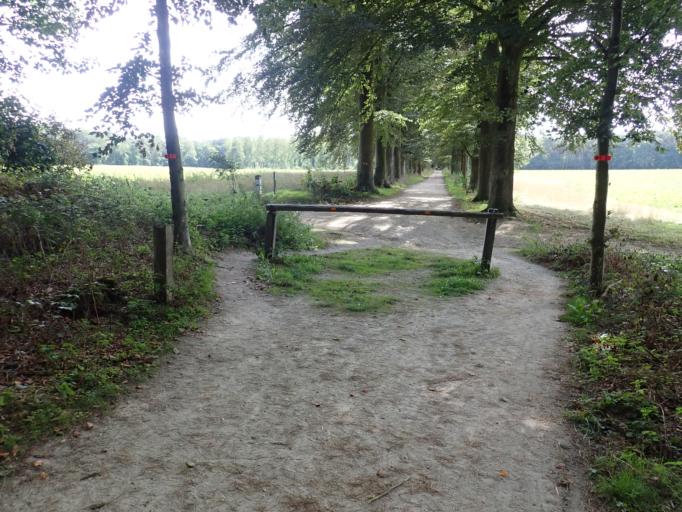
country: BE
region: Flanders
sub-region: Provincie Vlaams-Brabant
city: Oud-Heverlee
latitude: 50.8177
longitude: 4.6643
